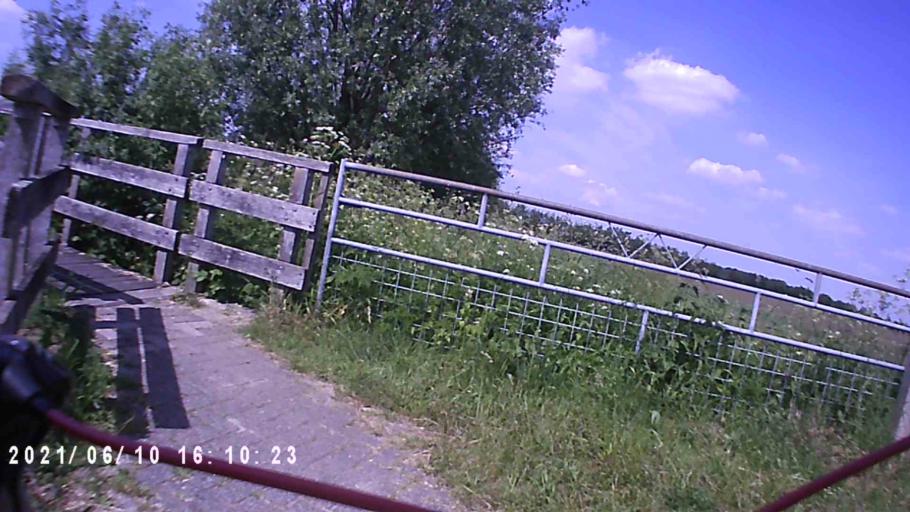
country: NL
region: Friesland
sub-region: Gemeente Tytsjerksteradiel
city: Eastermar
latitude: 53.2072
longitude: 6.0524
